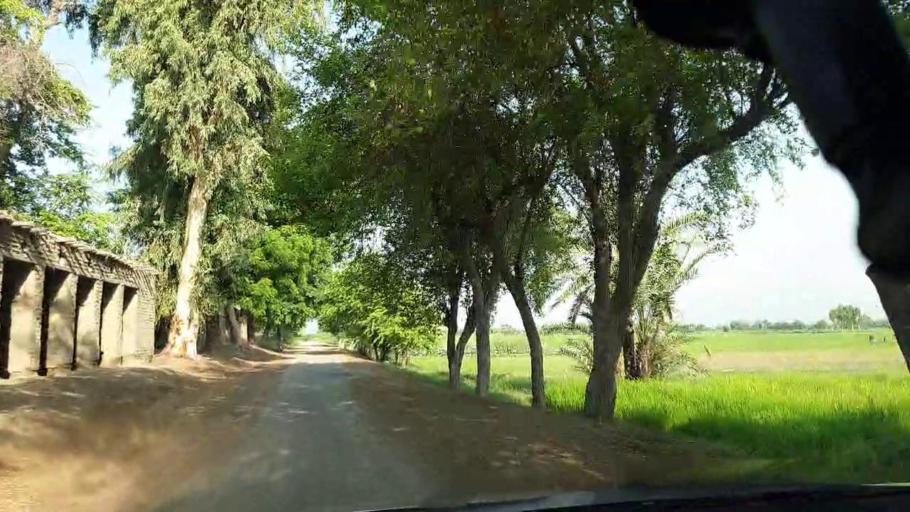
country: PK
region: Sindh
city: Larkana
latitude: 27.6199
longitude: 68.2118
